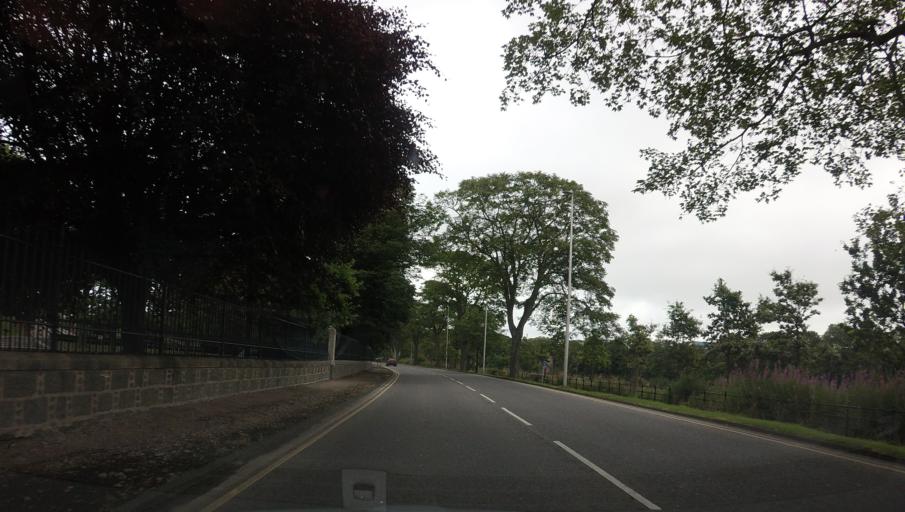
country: GB
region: Scotland
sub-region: Aberdeen City
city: Aberdeen
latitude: 57.1290
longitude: -2.1005
